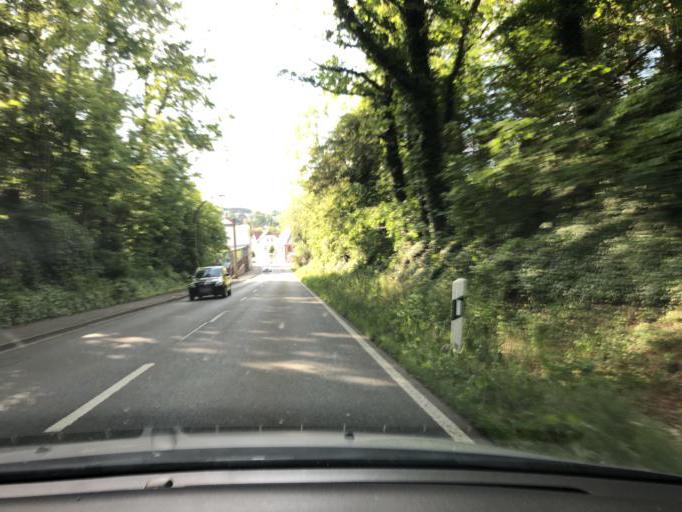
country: DE
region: Thuringia
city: Schmolln
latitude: 50.8960
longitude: 12.3605
